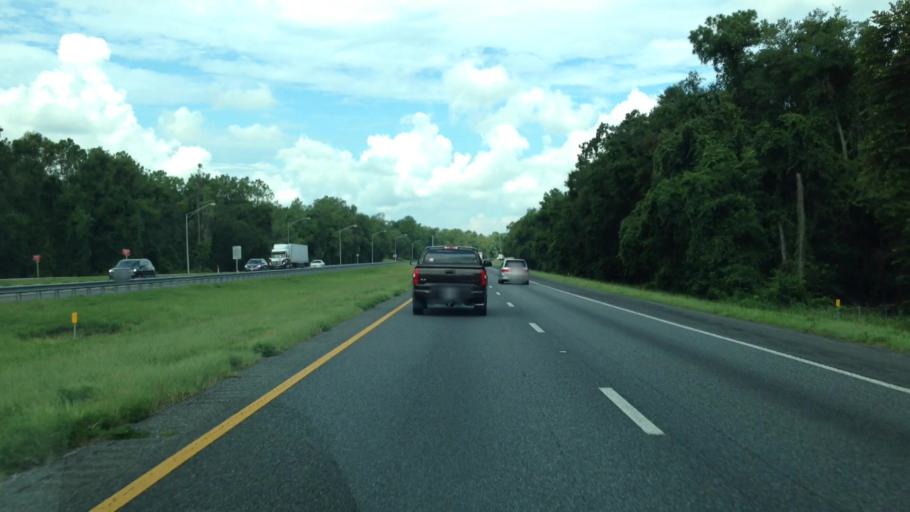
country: US
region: Florida
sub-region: Suwannee County
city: Wellborn
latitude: 30.2751
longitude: -82.8002
